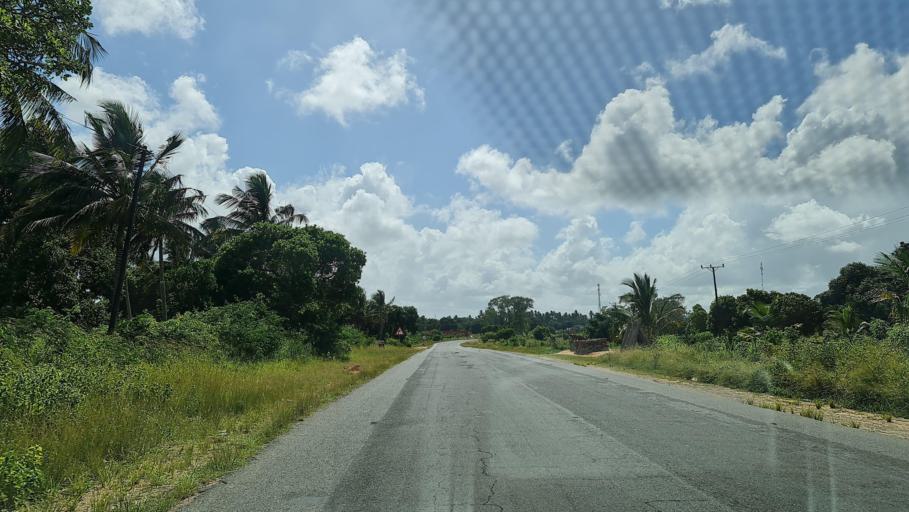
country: MZ
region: Gaza
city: Manjacaze
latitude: -24.6744
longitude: 34.5710
